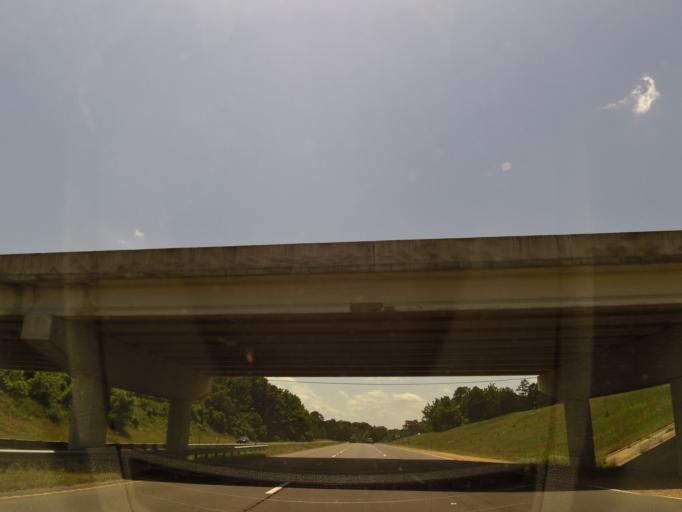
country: US
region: Mississippi
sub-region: Lafayette County
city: Oxford
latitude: 34.3559
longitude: -89.4976
